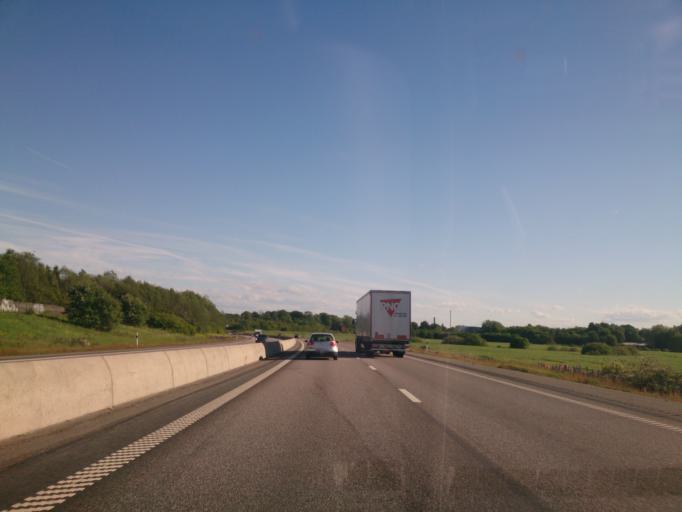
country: SE
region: OEstergoetland
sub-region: Norrkopings Kommun
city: Norrkoping
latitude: 58.6035
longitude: 16.1273
